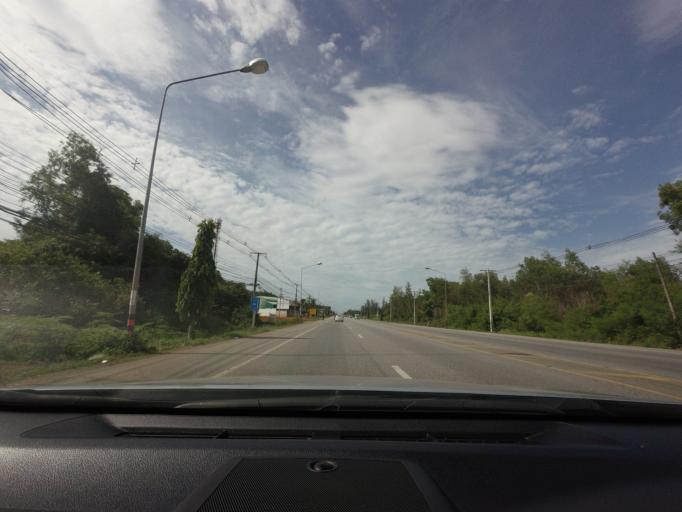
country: TH
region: Songkhla
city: Khlong Hoi Khong
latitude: 6.9543
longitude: 100.4198
